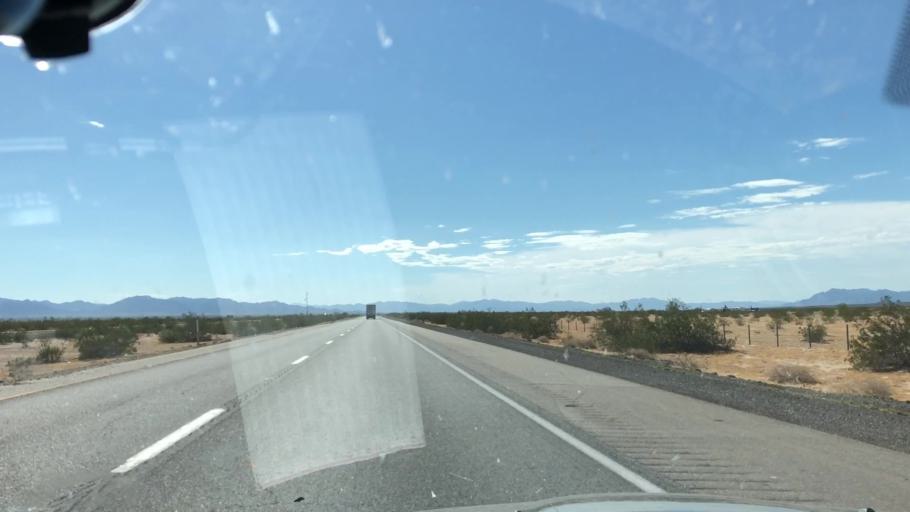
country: US
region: California
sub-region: Riverside County
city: Mesa Verde
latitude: 33.6277
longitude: -115.0616
